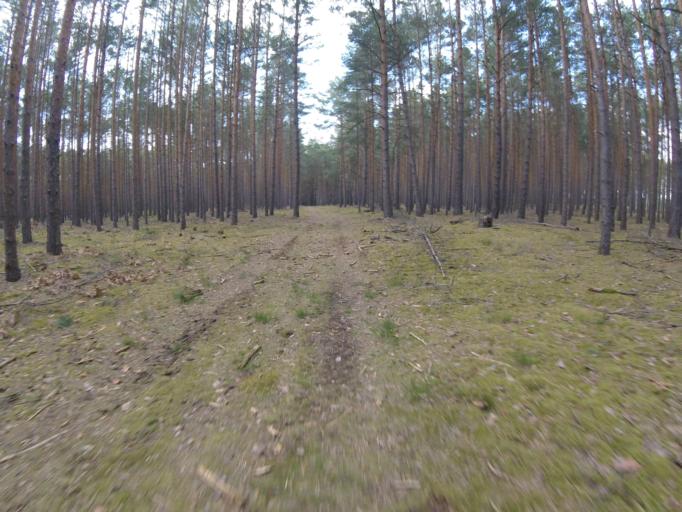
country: DE
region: Brandenburg
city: Bestensee
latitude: 52.2142
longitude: 13.6616
